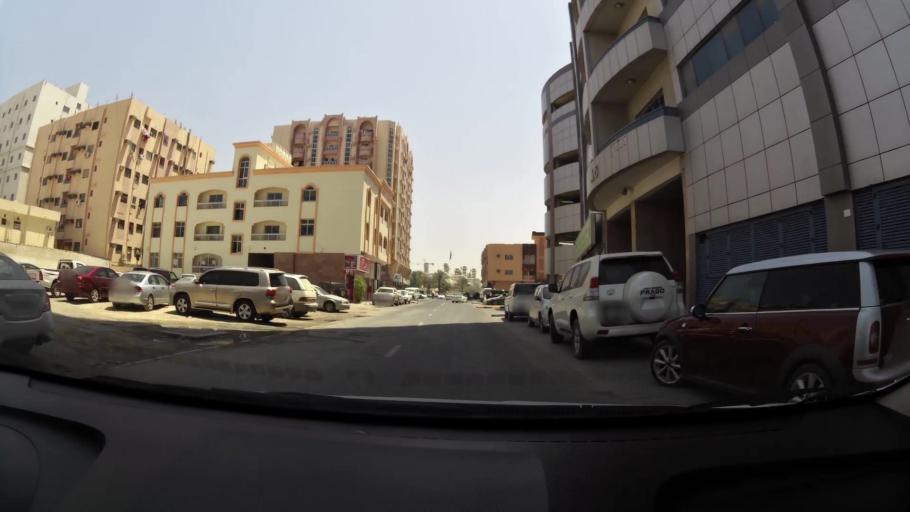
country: AE
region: Ajman
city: Ajman
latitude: 25.3999
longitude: 55.4481
